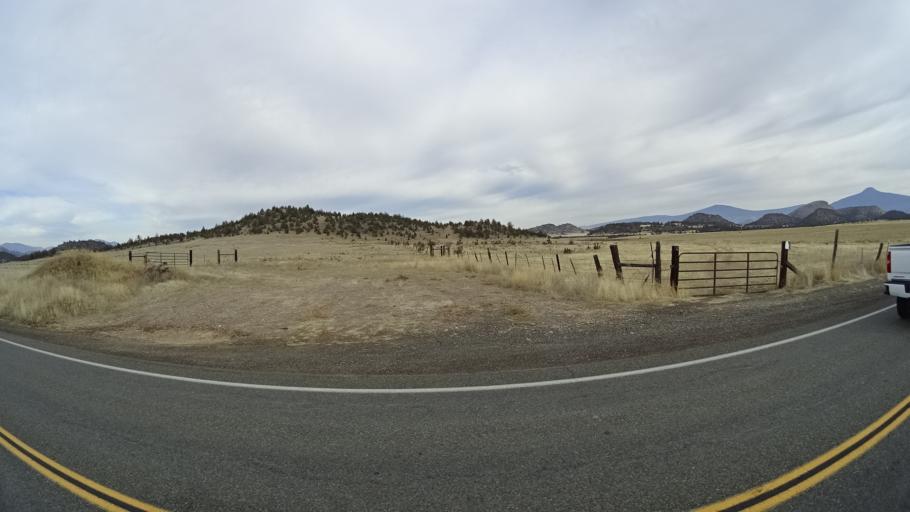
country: US
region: California
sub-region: Siskiyou County
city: Montague
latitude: 41.6405
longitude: -122.4763
